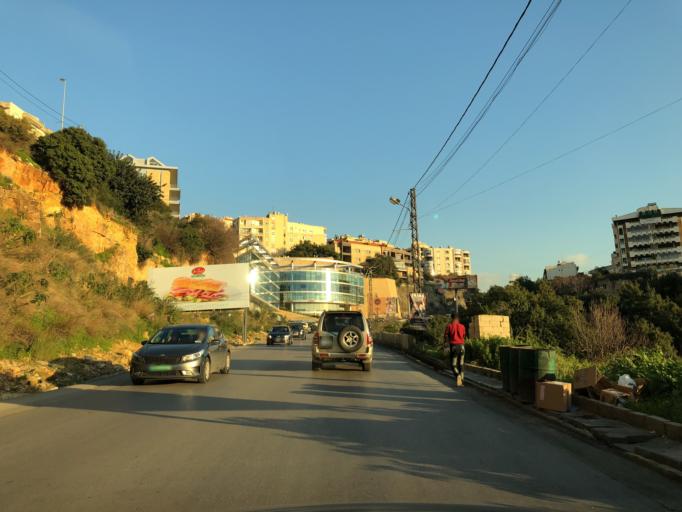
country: LB
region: Mont-Liban
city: Baabda
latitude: 33.8566
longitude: 35.5625
